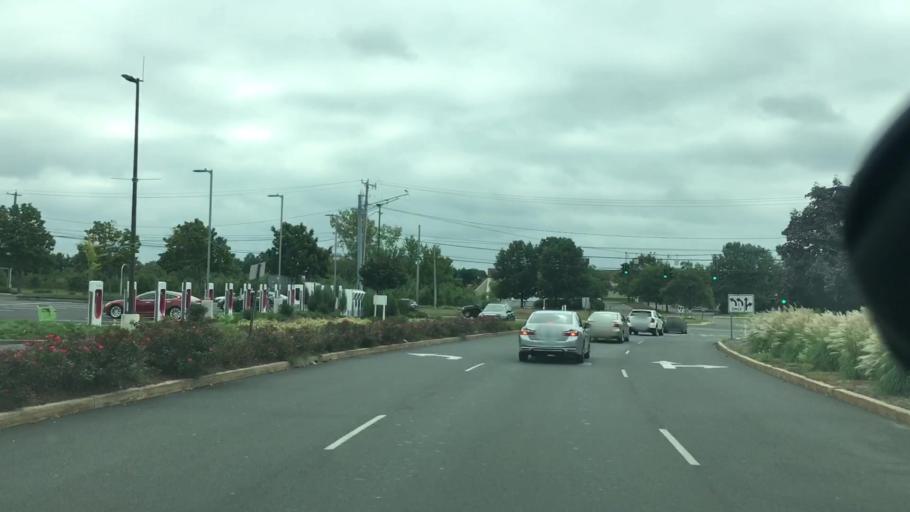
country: US
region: Connecticut
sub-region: Hartford County
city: Manchester
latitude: 41.8049
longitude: -72.5627
